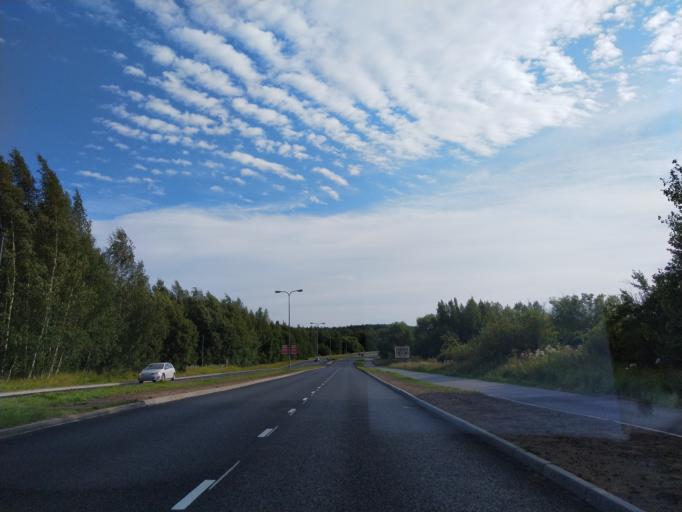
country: FI
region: Varsinais-Suomi
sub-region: Turku
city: Turku
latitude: 60.4266
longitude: 22.2397
